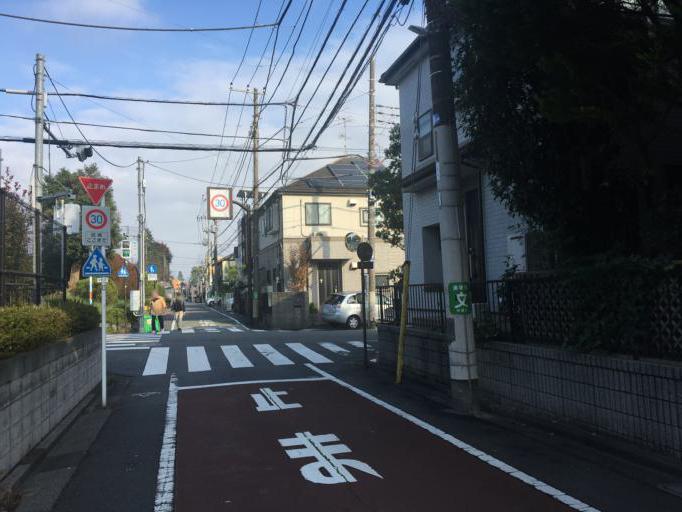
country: JP
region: Tokyo
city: Musashino
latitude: 35.7207
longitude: 139.6011
